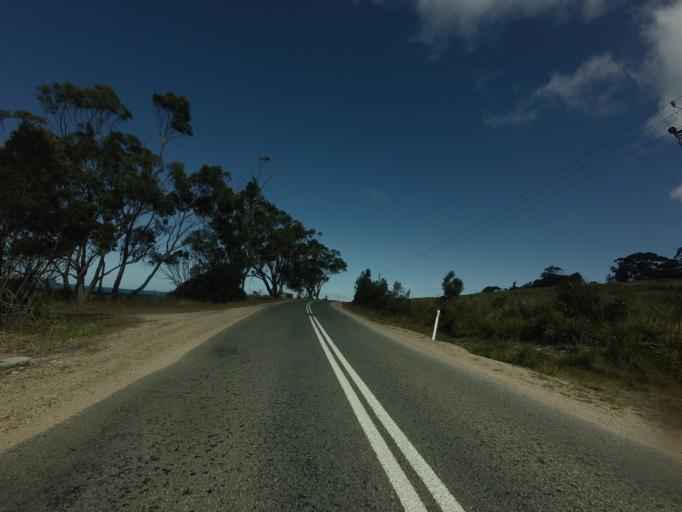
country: AU
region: Tasmania
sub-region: Break O'Day
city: St Helens
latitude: -41.7852
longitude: 148.2604
